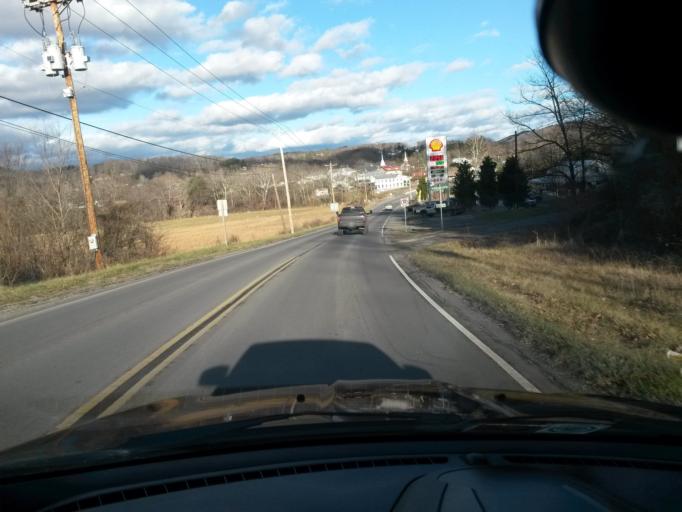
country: US
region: Virginia
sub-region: Giles County
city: Narrows
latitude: 37.3958
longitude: -80.8038
